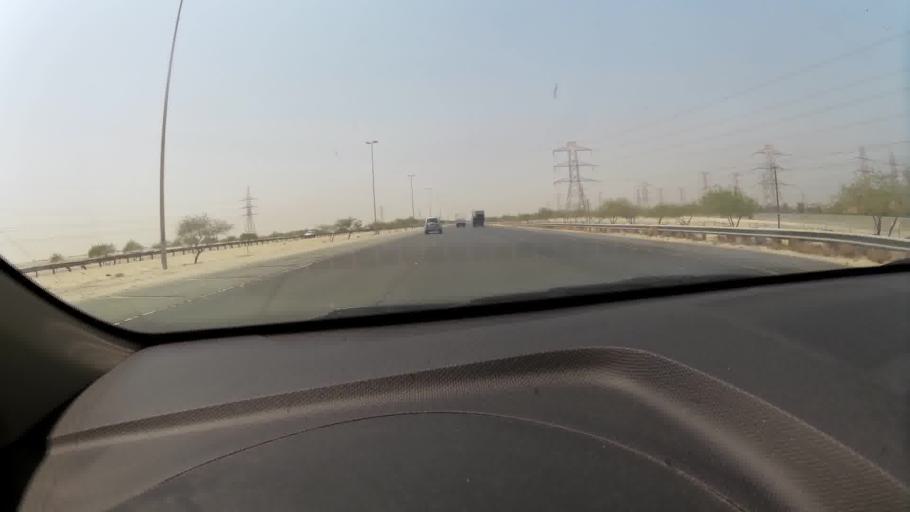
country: KW
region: Al Ahmadi
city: Al Fahahil
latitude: 28.9432
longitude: 48.1435
